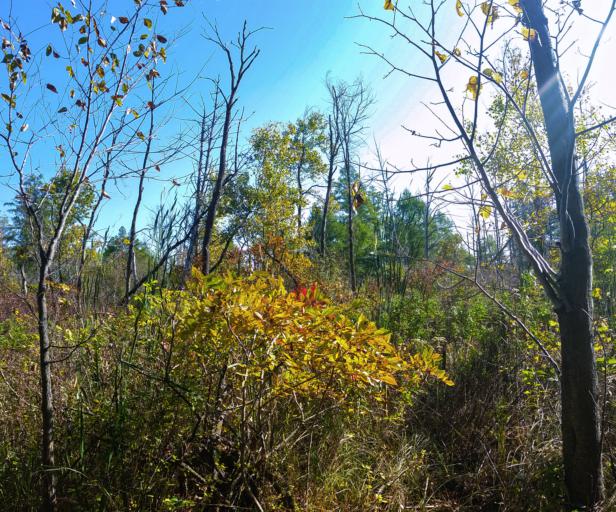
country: US
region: Wisconsin
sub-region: Jefferson County
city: Lake Mills
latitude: 43.0569
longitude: -88.9483
